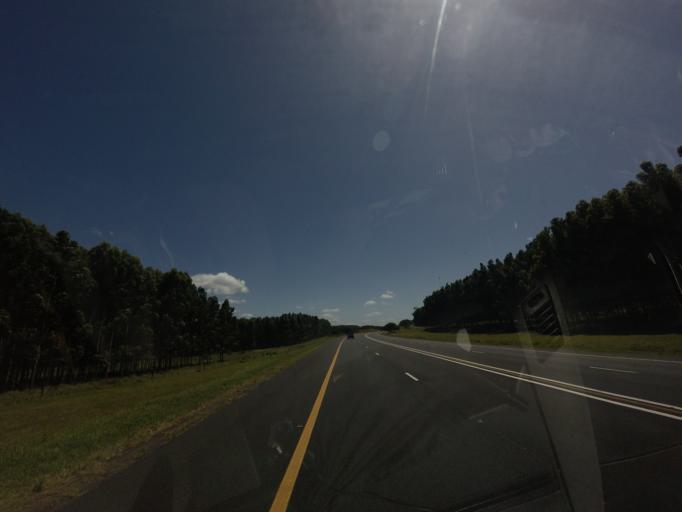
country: ZA
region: KwaZulu-Natal
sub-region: uThungulu District Municipality
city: Eshowe
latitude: -29.0164
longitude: 31.6756
